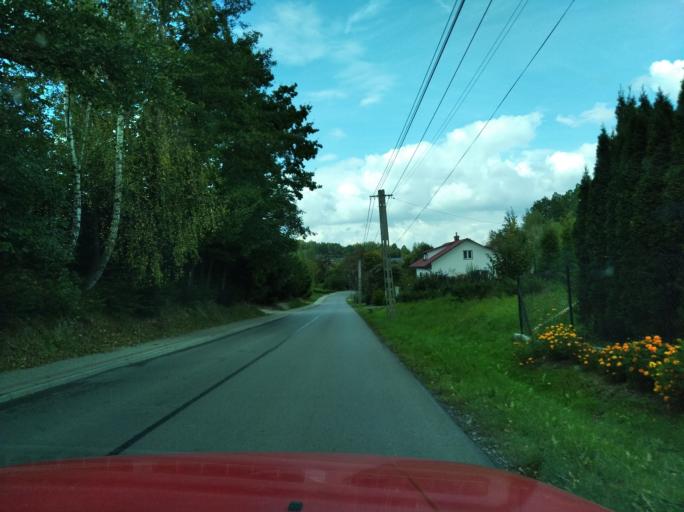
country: PL
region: Subcarpathian Voivodeship
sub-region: Powiat rzeszowski
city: Tyczyn
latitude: 49.9377
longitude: 22.0209
